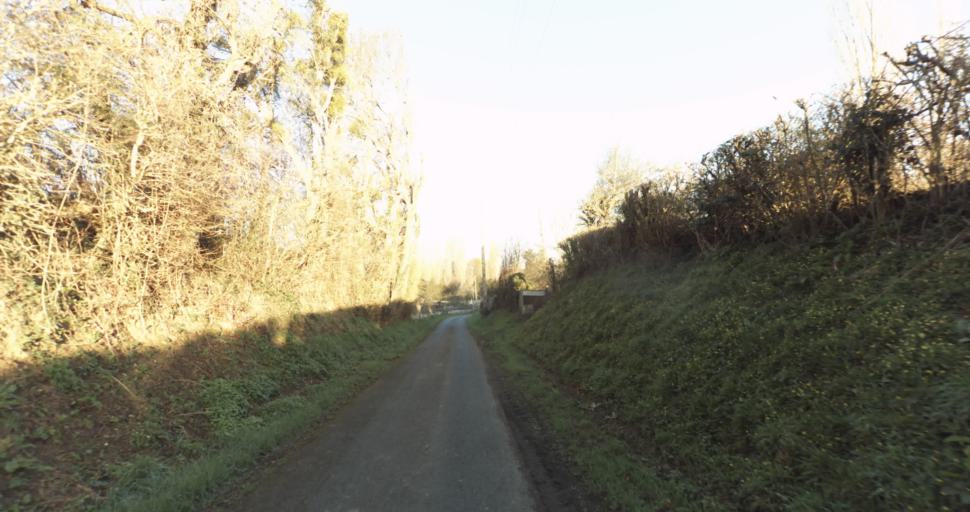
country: FR
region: Lower Normandy
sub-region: Departement du Calvados
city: Saint-Pierre-sur-Dives
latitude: 49.0293
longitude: -0.0238
